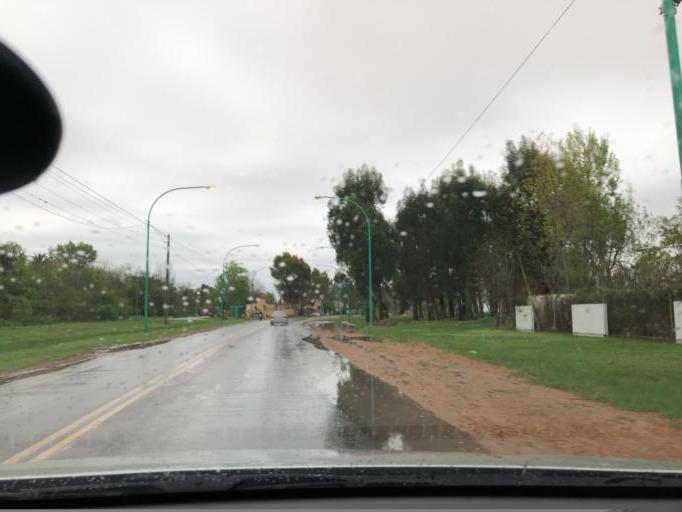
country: AR
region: Buenos Aires
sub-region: Partido de Ensenada
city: Ensenada
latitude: -34.8310
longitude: -57.9539
